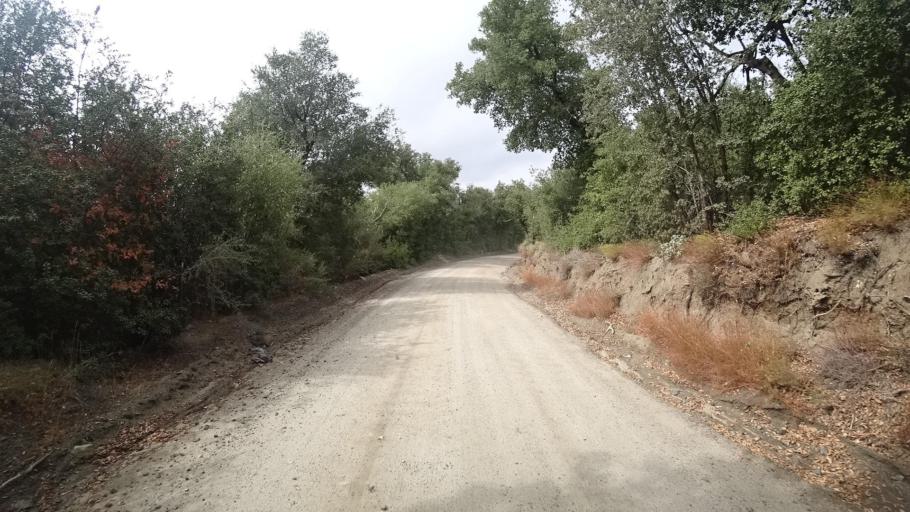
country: US
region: California
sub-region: San Diego County
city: Descanso
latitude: 32.9554
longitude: -116.6402
